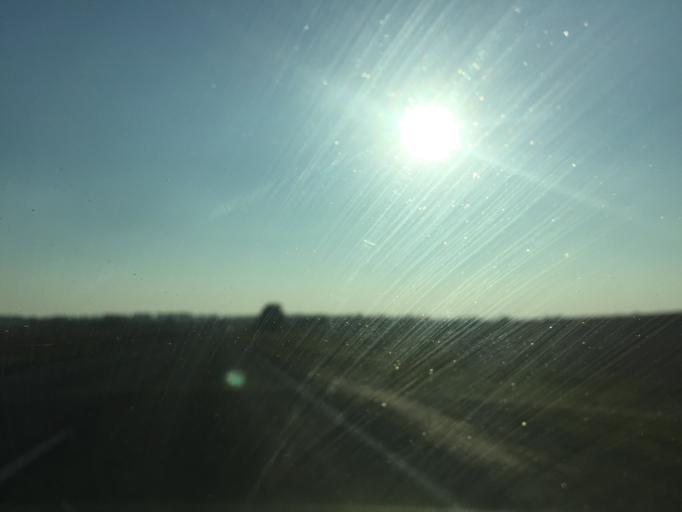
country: BY
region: Gomel
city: Dobrush
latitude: 52.3105
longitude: 31.2411
